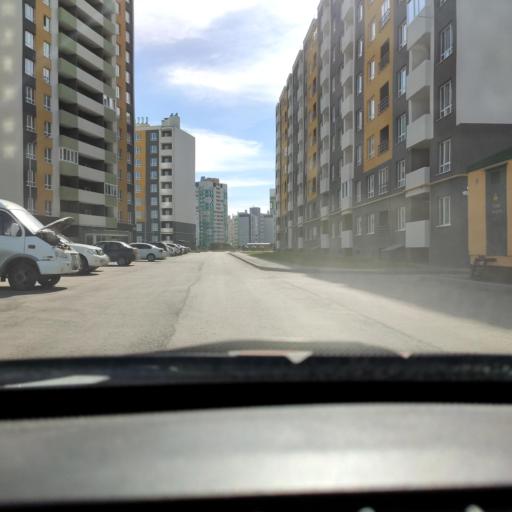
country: RU
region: Samara
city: Samara
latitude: 53.0990
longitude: 50.1713
